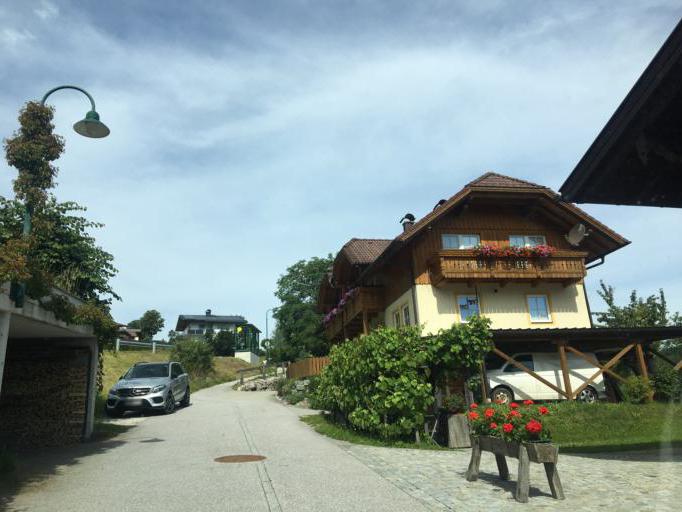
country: AT
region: Styria
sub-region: Politischer Bezirk Liezen
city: Schladming
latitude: 47.3856
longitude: 13.6768
